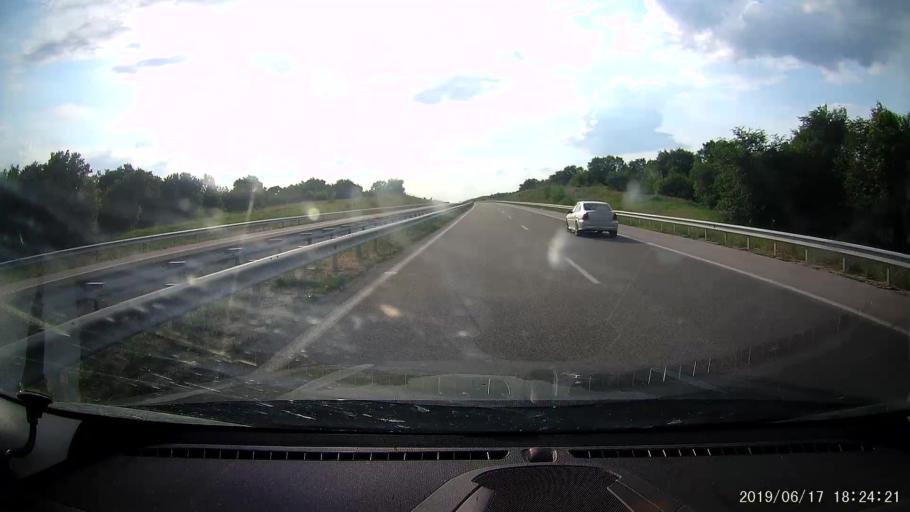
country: BG
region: Khaskovo
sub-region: Obshtina Dimitrovgrad
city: Dimitrovgrad
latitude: 41.9837
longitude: 25.6939
